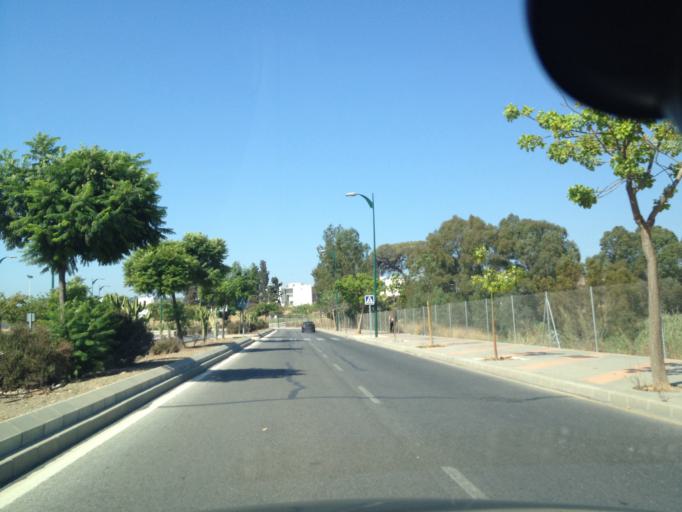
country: ES
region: Andalusia
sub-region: Provincia de Malaga
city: Malaga
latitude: 36.7249
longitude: -4.4897
